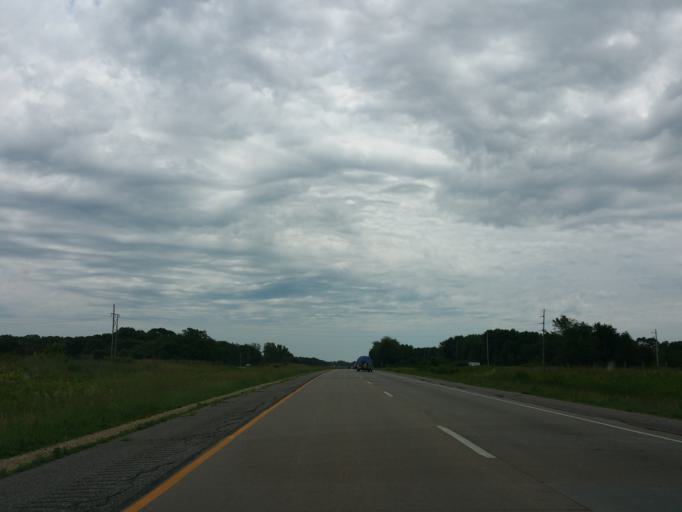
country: US
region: Wisconsin
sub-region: Juneau County
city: Mauston
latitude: 43.8399
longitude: -90.0951
